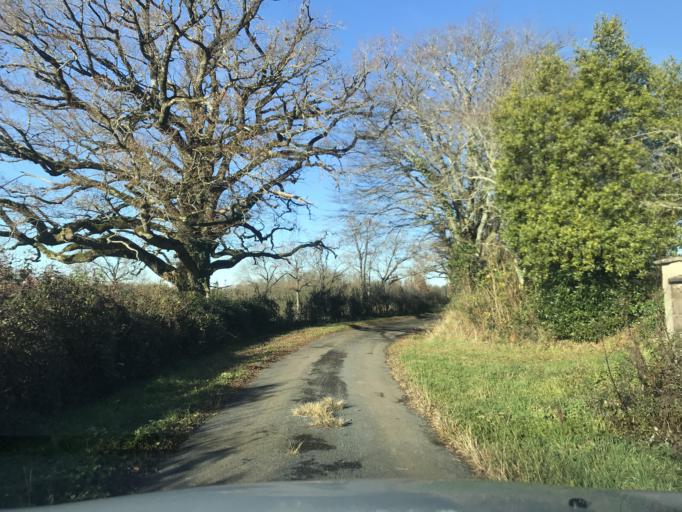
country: FR
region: Poitou-Charentes
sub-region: Departement de la Charente
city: Saint-Claud
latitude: 45.8508
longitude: 0.5134
